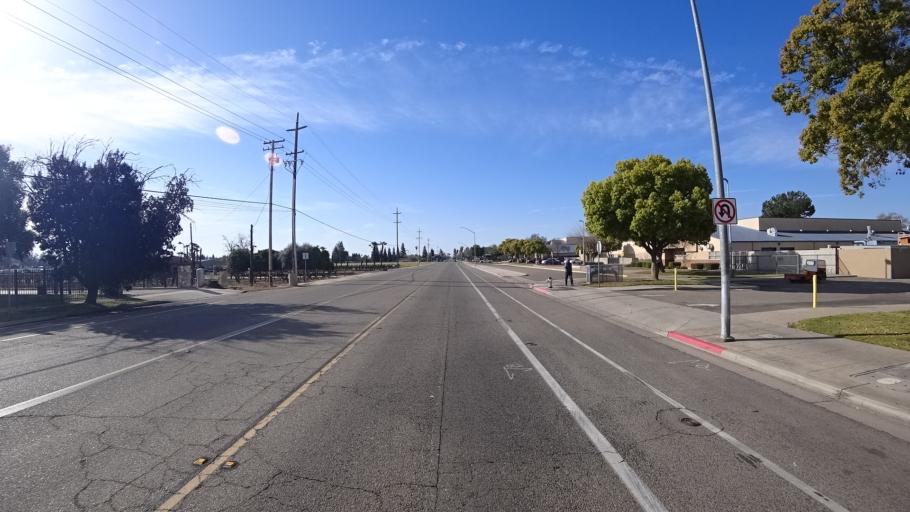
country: US
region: California
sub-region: Fresno County
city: West Park
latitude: 36.7893
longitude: -119.8805
